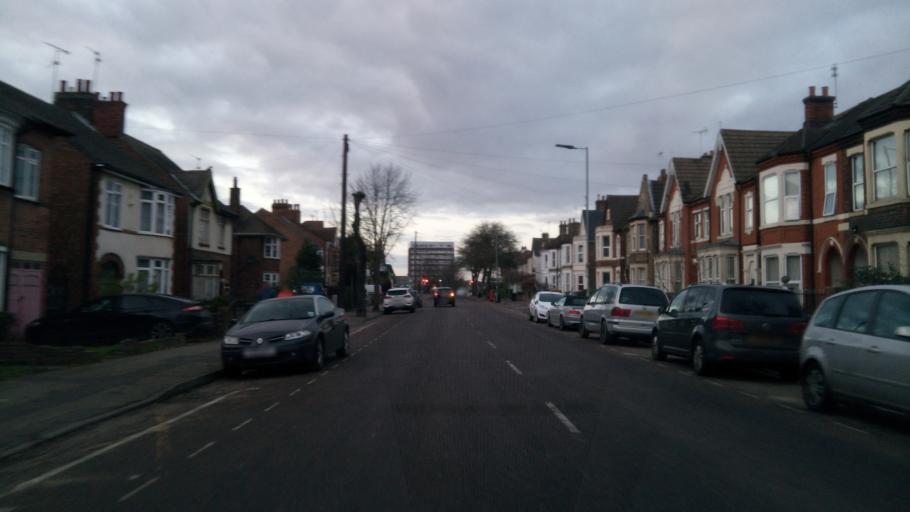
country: GB
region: England
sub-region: Peterborough
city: Peterborough
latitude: 52.5624
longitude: -0.2421
